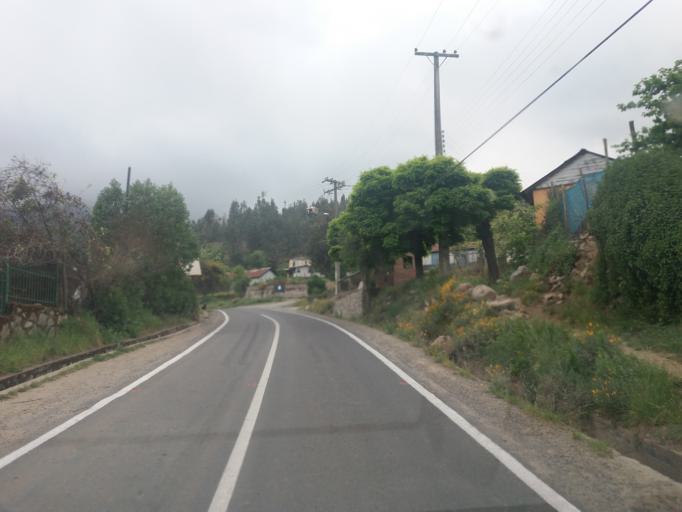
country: CL
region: Valparaiso
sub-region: Provincia de Marga Marga
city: Limache
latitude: -33.0481
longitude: -71.0993
